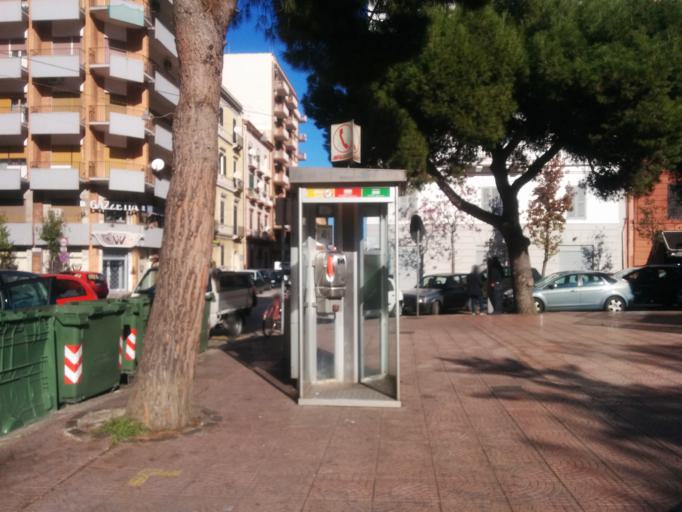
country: IT
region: Apulia
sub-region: Provincia di Taranto
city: Taranto
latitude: 40.4732
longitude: 17.2374
